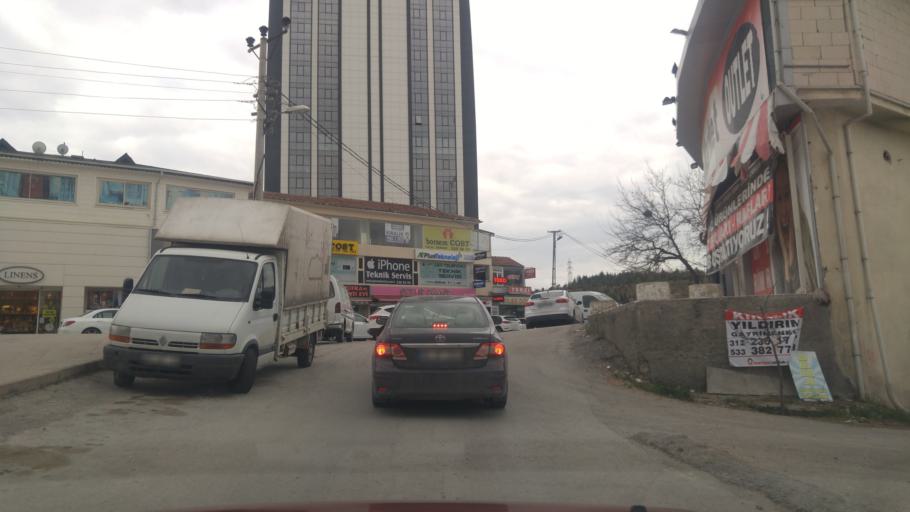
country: TR
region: Ankara
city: Batikent
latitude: 39.8864
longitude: 32.6951
